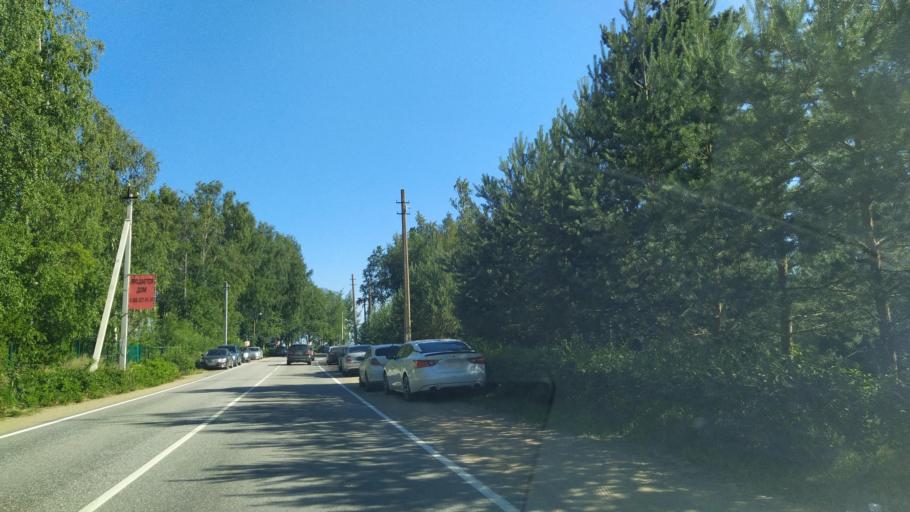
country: RU
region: Leningrad
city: Borisova Griva
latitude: 60.1158
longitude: 31.0820
